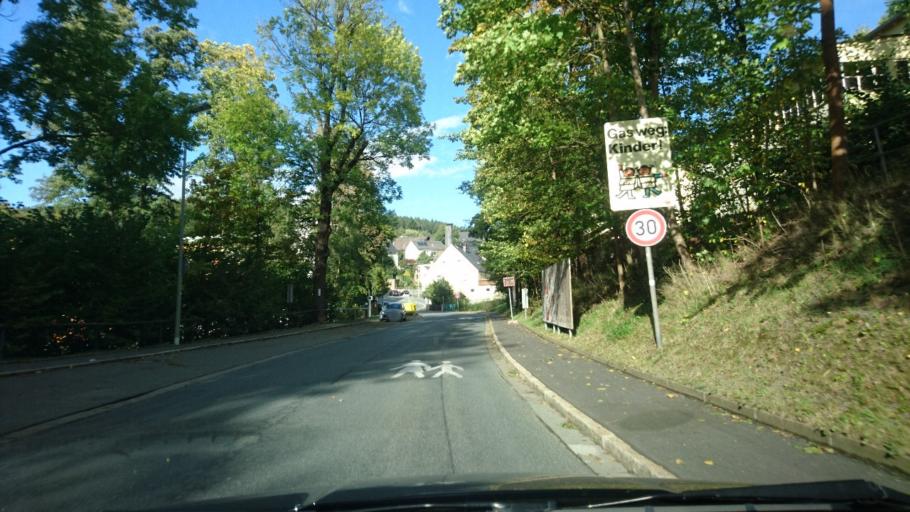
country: DE
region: Bavaria
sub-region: Upper Franconia
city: Naila
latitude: 50.3353
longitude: 11.7090
